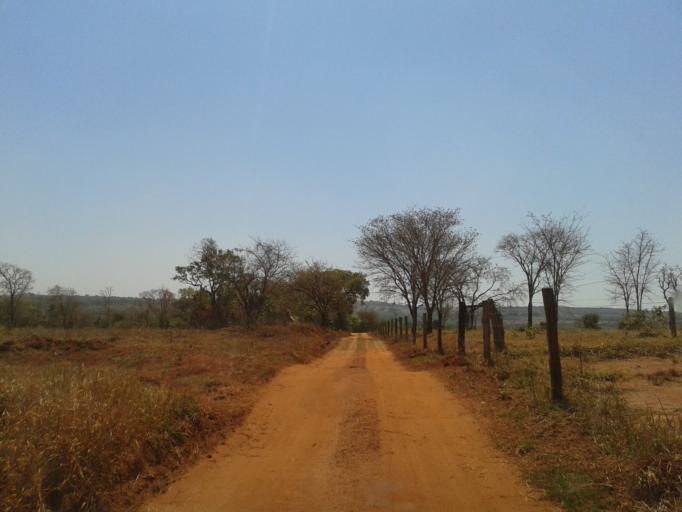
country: BR
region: Minas Gerais
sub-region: Ituiutaba
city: Ituiutaba
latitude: -19.0478
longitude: -49.3757
